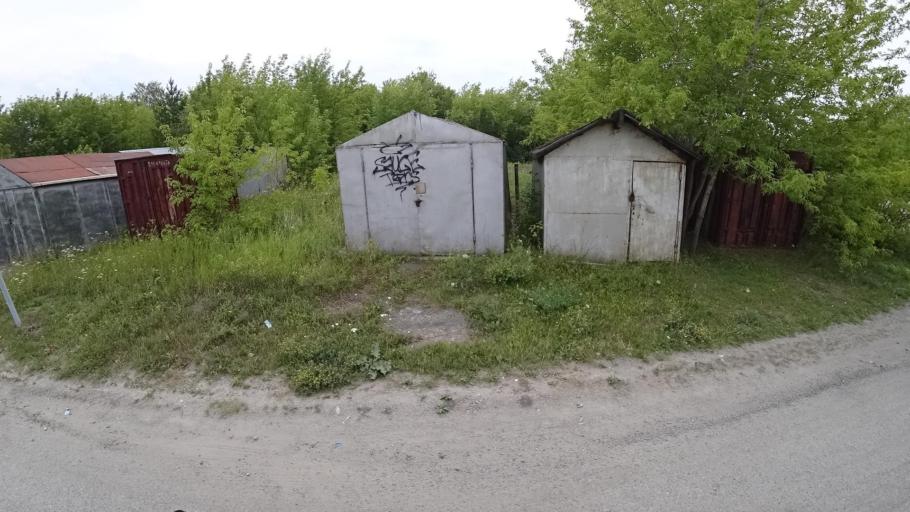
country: RU
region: Sverdlovsk
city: Kamyshlov
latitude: 56.8447
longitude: 62.7440
